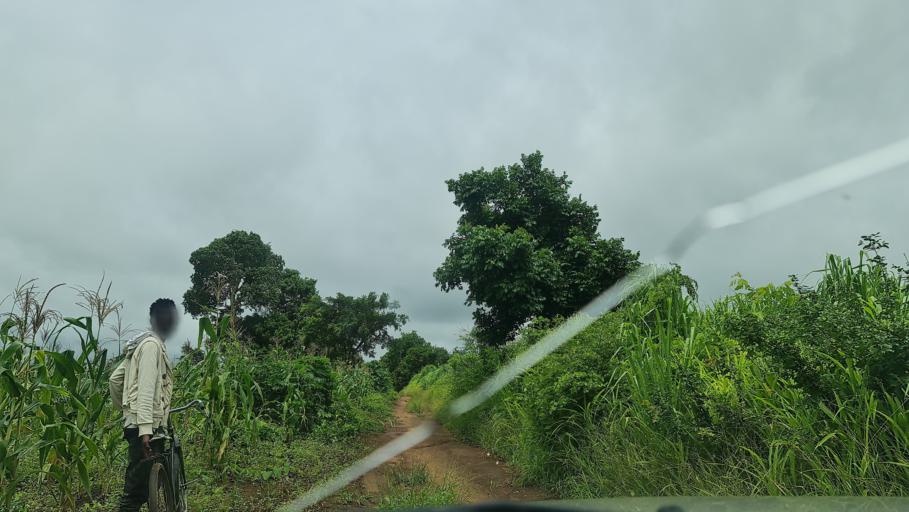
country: MW
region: Southern Region
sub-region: Nsanje District
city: Nsanje
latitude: -17.3827
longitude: 35.7774
